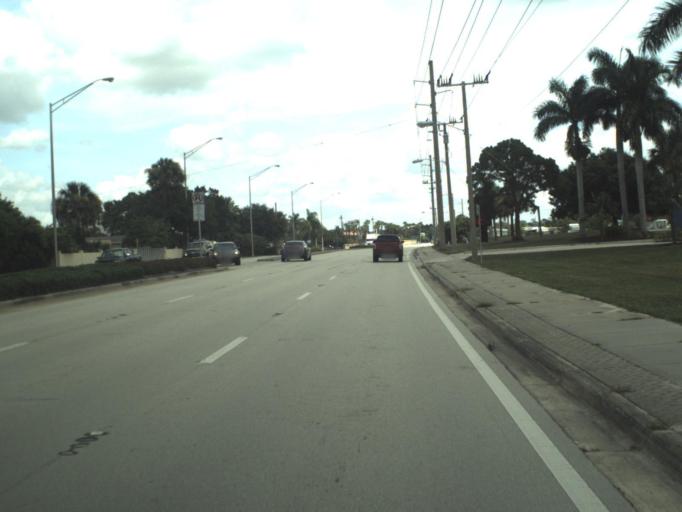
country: US
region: Florida
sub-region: Martin County
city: Palm City
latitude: 27.1696
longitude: -80.2514
